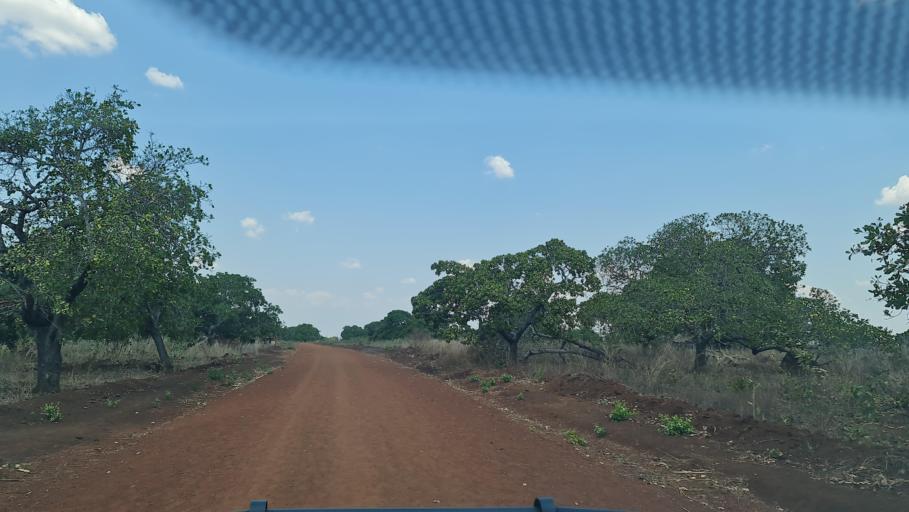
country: MZ
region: Nampula
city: Nacala
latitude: -14.8132
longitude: 40.0744
